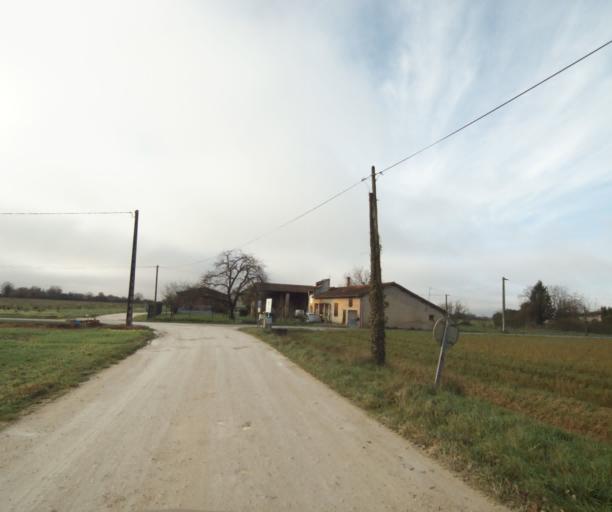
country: FR
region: Midi-Pyrenees
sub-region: Departement de la Haute-Garonne
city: Villemur-sur-Tarn
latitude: 43.8746
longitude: 1.4903
